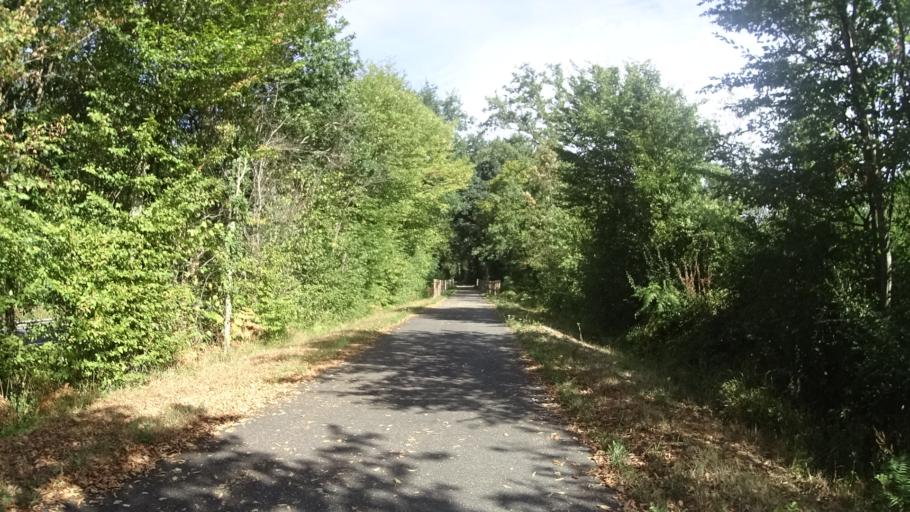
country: FR
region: Bourgogne
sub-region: Departement de Saone-et-Loire
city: Bourbon-Lancy
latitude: 46.6184
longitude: 3.7407
